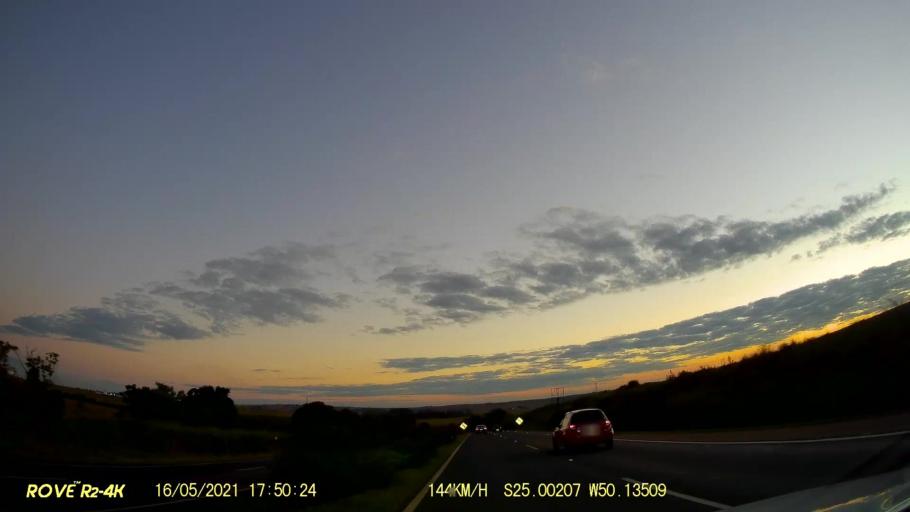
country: BR
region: Parana
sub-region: Carambei
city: Carambei
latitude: -25.0021
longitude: -50.1352
